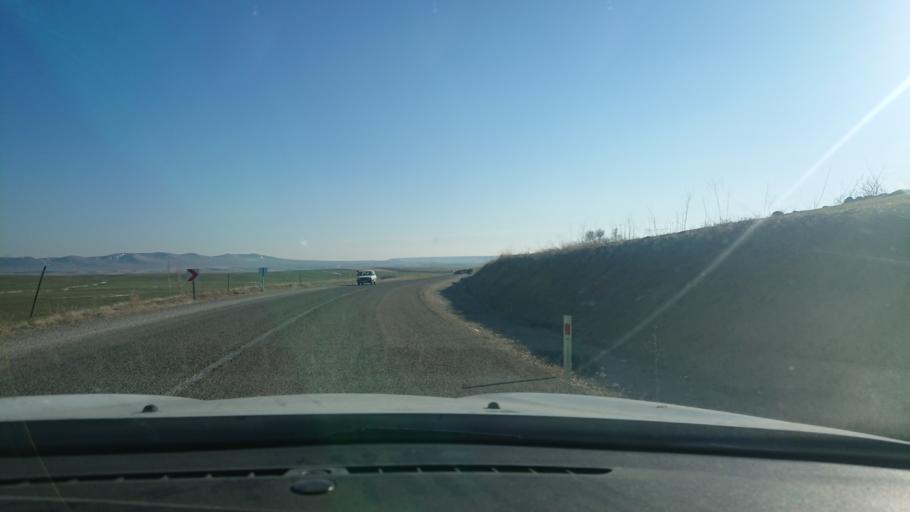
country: TR
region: Aksaray
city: Agacoren
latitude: 38.8269
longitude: 33.8879
